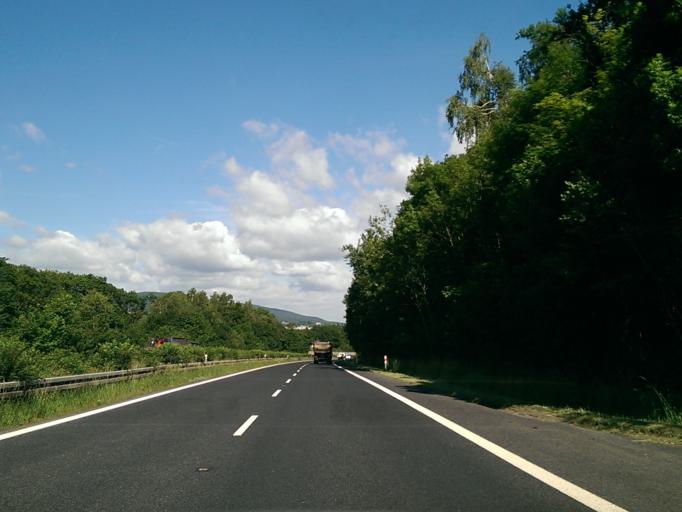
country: CZ
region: Liberecky
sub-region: Okres Liberec
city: Liberec
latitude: 50.7229
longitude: 15.0643
